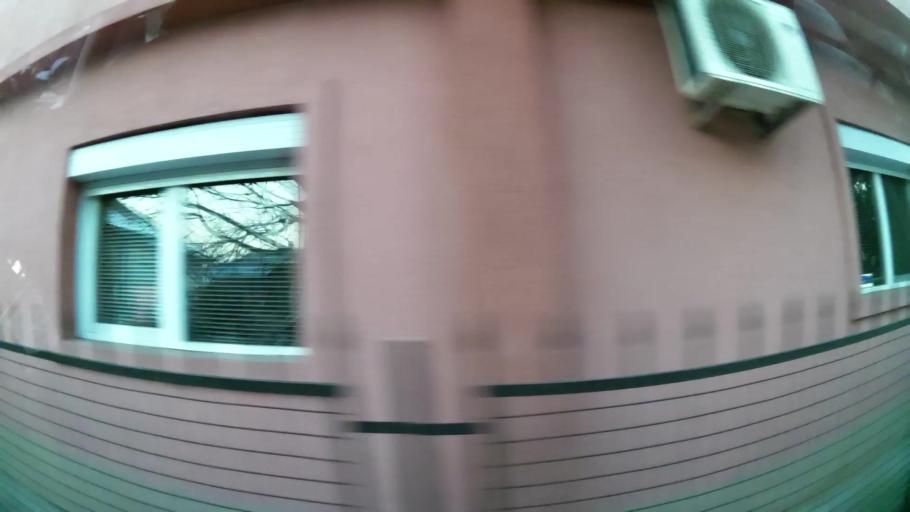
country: MK
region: Kisela Voda
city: Usje
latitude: 41.9816
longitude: 21.4855
